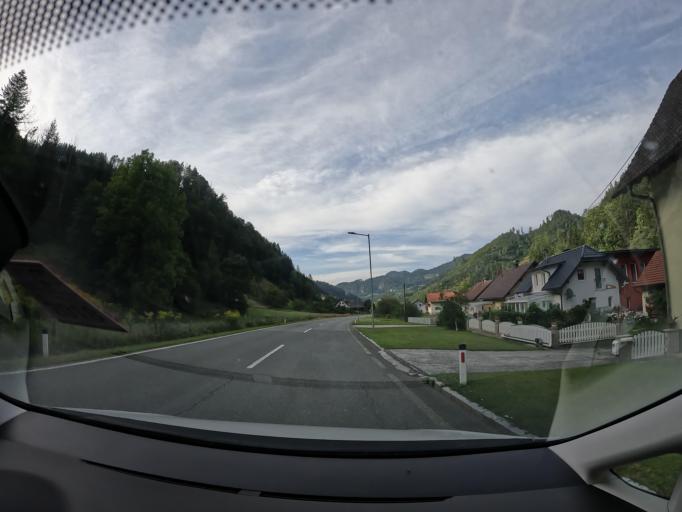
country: AT
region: Carinthia
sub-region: Politischer Bezirk Volkermarkt
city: Bad Eisenkappel
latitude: 46.4679
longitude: 14.5925
